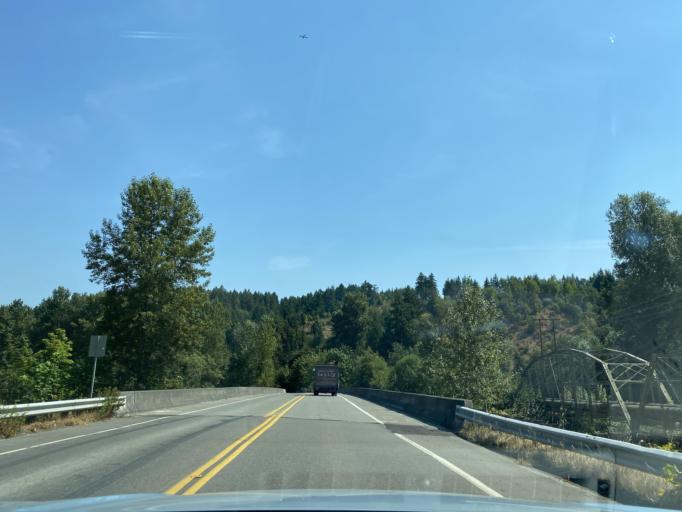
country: US
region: Washington
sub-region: Pierce County
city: McMillin
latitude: 47.1400
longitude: -122.2278
